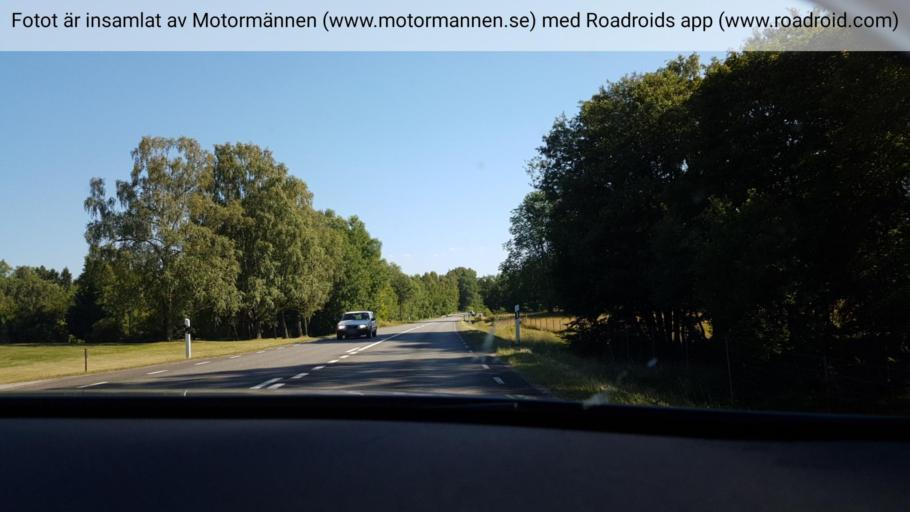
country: SE
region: Vaestra Goetaland
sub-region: Skara Kommun
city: Skara
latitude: 58.3386
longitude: 13.4359
